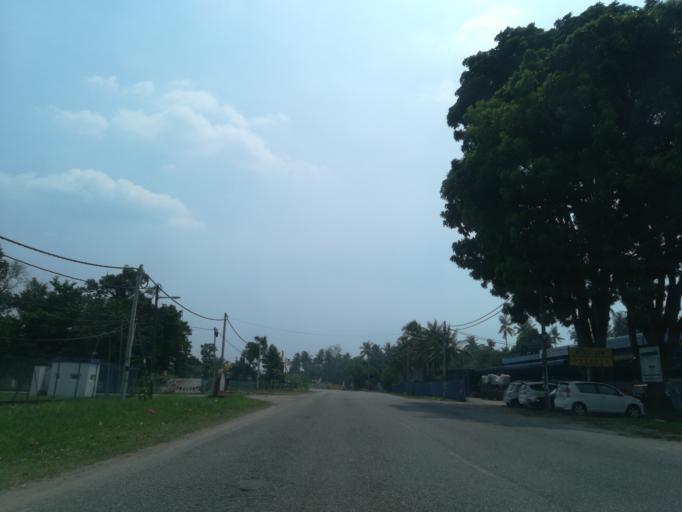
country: MY
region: Penang
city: Tasek Glugor
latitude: 5.4345
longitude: 100.5363
